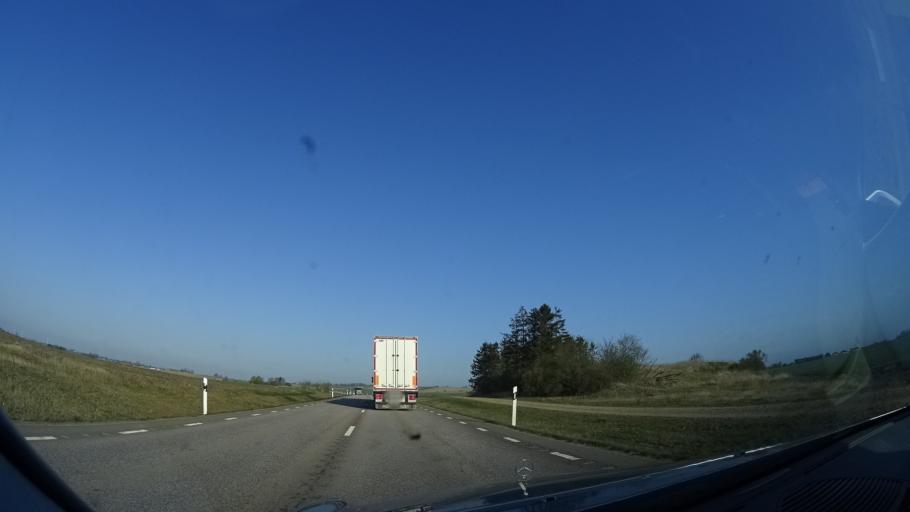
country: SE
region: Skane
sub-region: Eslovs Kommun
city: Eslov
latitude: 55.8661
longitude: 13.2259
